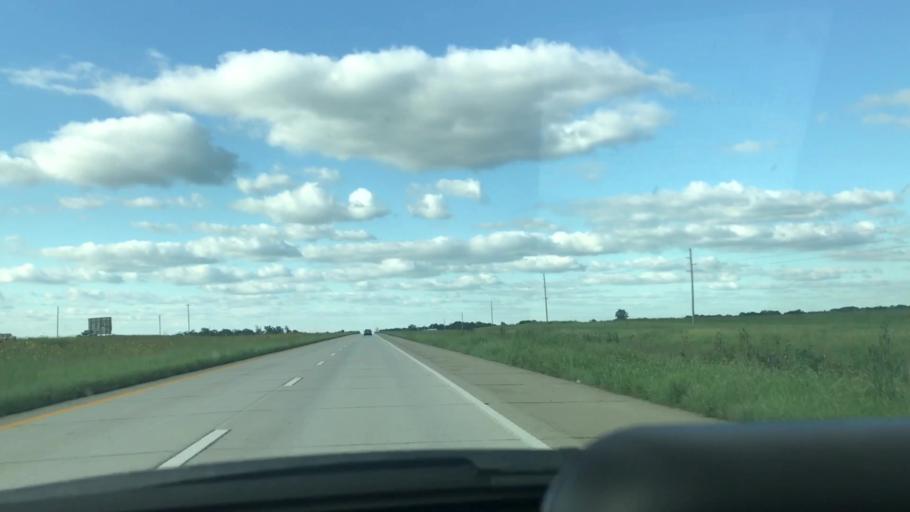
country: US
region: Missouri
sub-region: Benton County
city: Cole Camp
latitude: 38.5137
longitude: -93.2726
